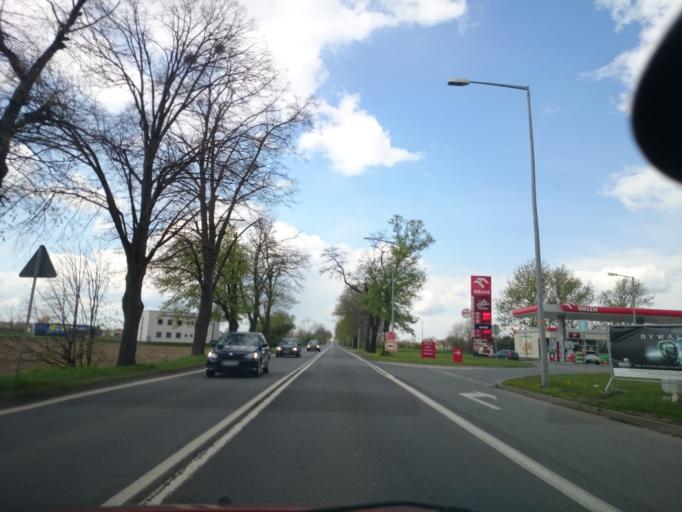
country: PL
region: Opole Voivodeship
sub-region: Powiat opolski
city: Opole
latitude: 50.6497
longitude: 17.9729
